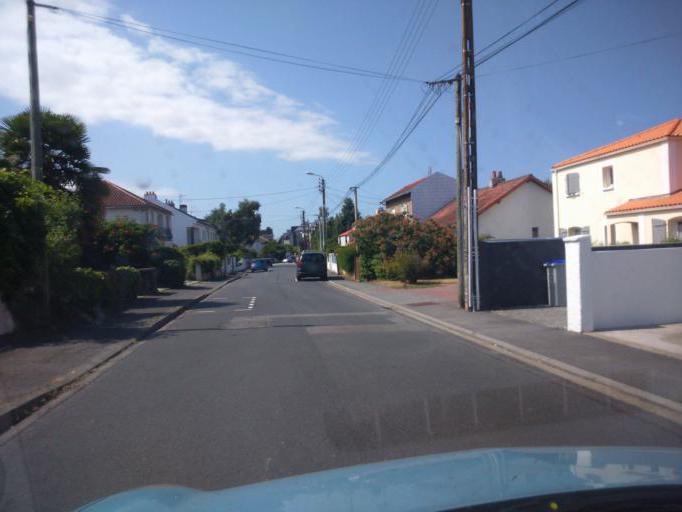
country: FR
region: Pays de la Loire
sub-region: Departement de la Loire-Atlantique
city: Saint-Sebastien-sur-Loire
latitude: 47.2009
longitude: -1.5215
